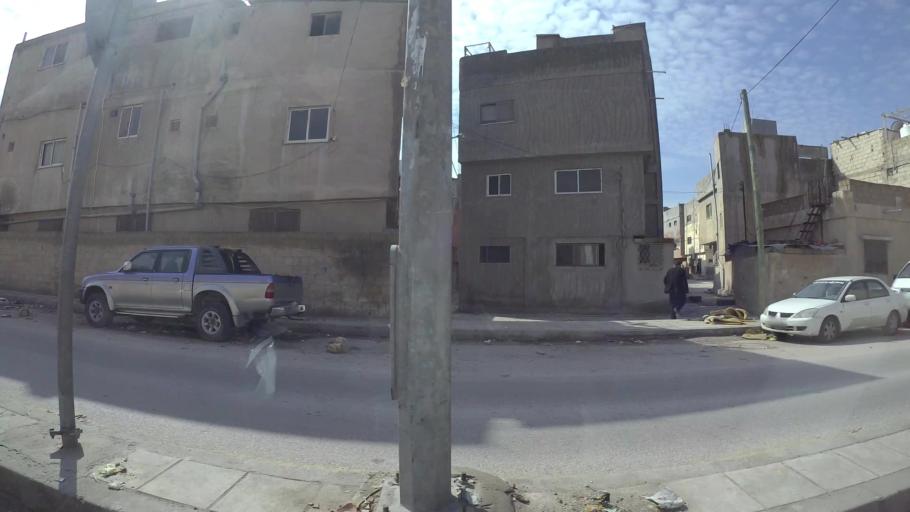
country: JO
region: Amman
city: Al Jubayhah
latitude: 32.0781
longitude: 35.8400
